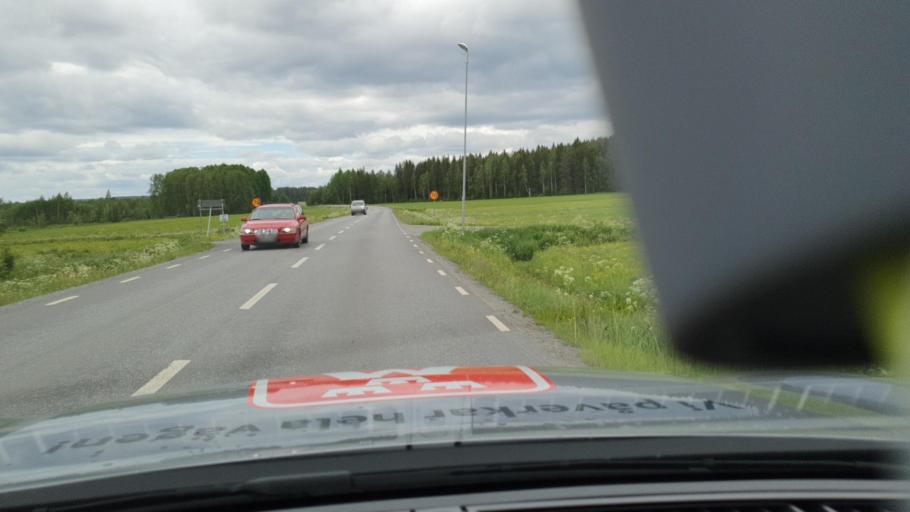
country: SE
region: Norrbotten
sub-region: Lulea Kommun
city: Sodra Sunderbyn
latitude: 65.8160
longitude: 22.0035
